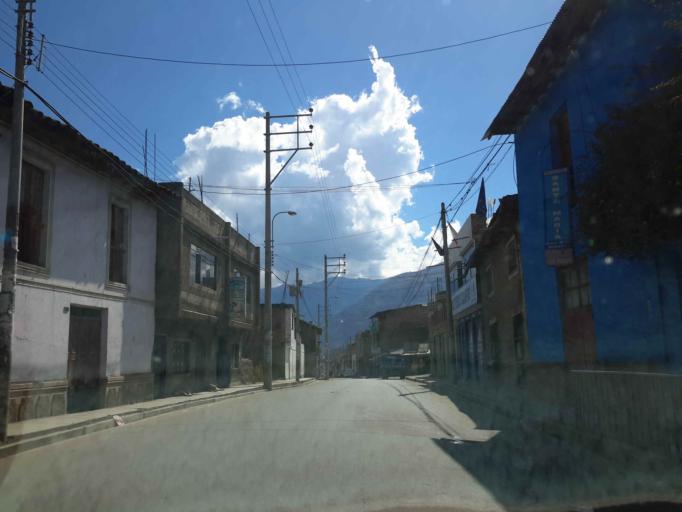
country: PE
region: Apurimac
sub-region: Provincia de Andahuaylas
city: Talavera
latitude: -13.6546
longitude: -73.4248
